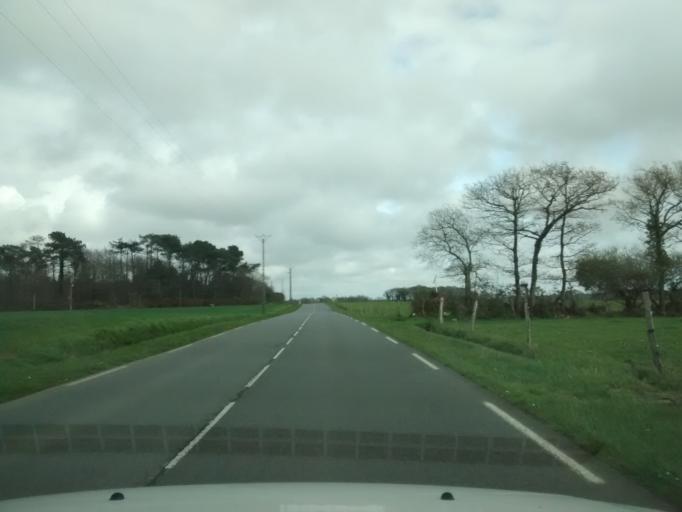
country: FR
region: Brittany
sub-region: Departement du Finistere
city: Clohars-Carnoet
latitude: 47.7978
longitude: -3.5469
